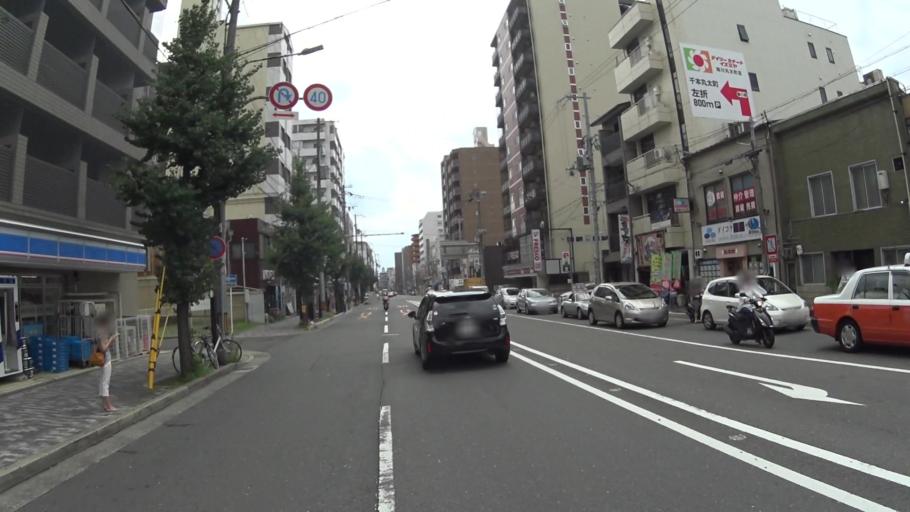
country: JP
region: Kyoto
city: Kyoto
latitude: 35.0180
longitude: 135.7427
